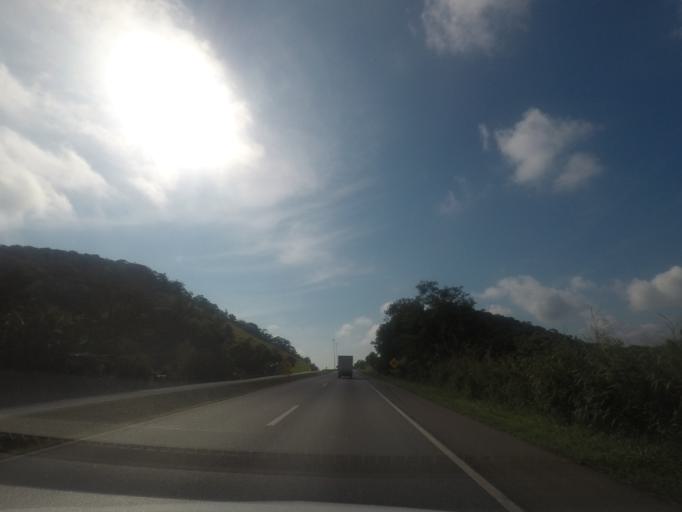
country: BR
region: Parana
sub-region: Antonina
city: Antonina
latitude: -25.5344
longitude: -48.7595
